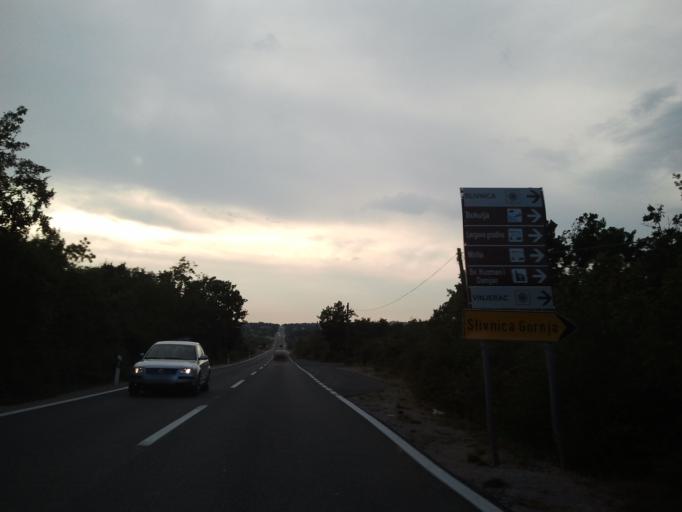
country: HR
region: Zadarska
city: Posedarje
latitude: 44.2276
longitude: 15.4301
